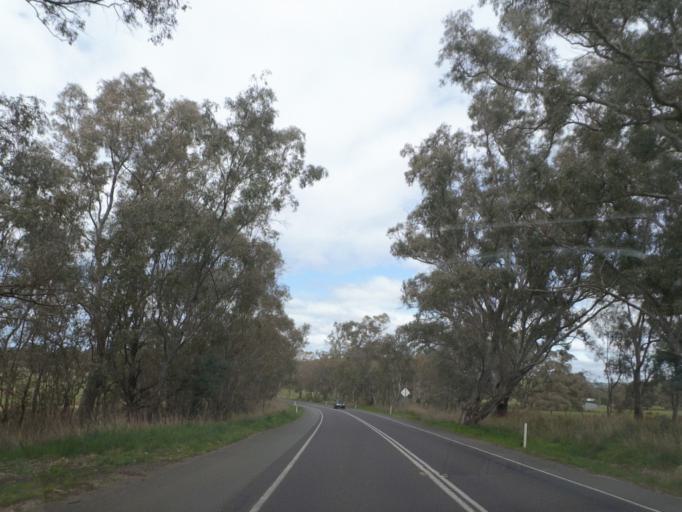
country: AU
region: Victoria
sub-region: Murrindindi
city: Kinglake West
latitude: -37.1620
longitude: 145.2920
